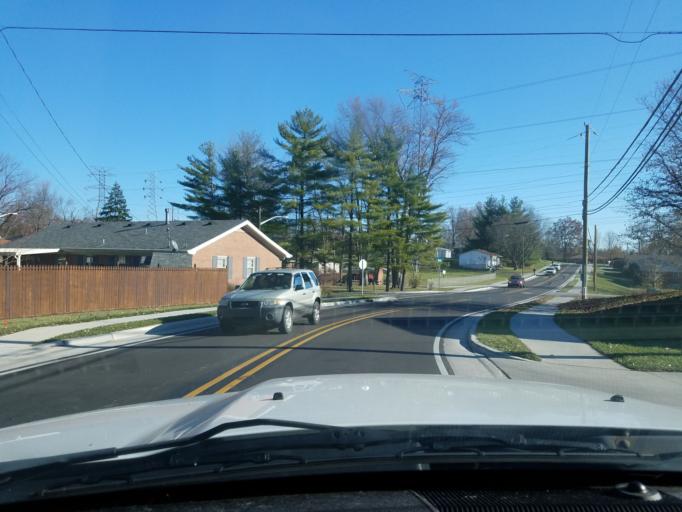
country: US
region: Indiana
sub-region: Floyd County
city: New Albany
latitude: 38.3228
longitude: -85.8154
